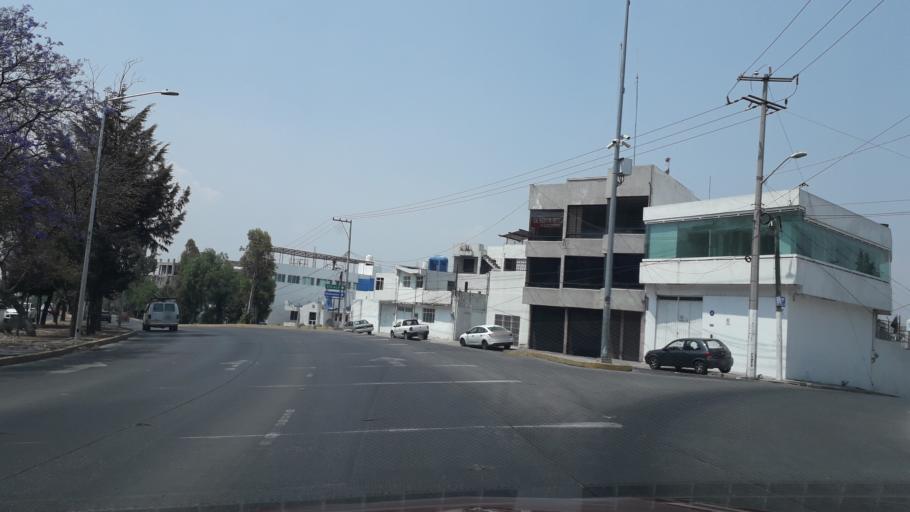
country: MX
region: Puebla
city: Puebla
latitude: 19.0594
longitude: -98.1878
